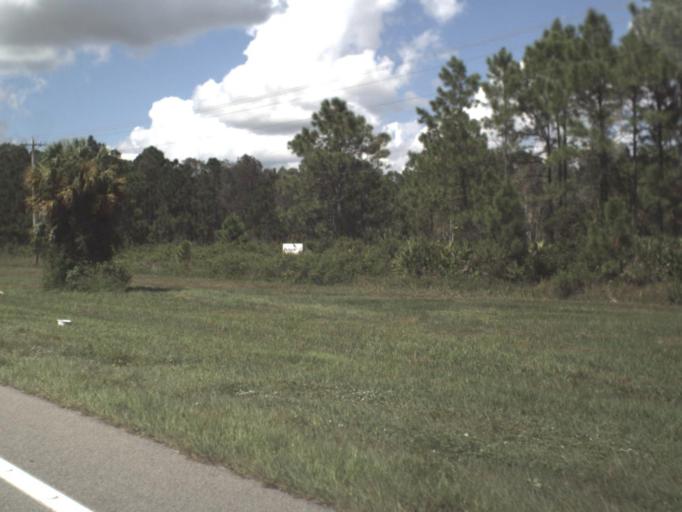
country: US
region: Florida
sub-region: Lee County
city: Lehigh Acres
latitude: 26.5339
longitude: -81.6245
